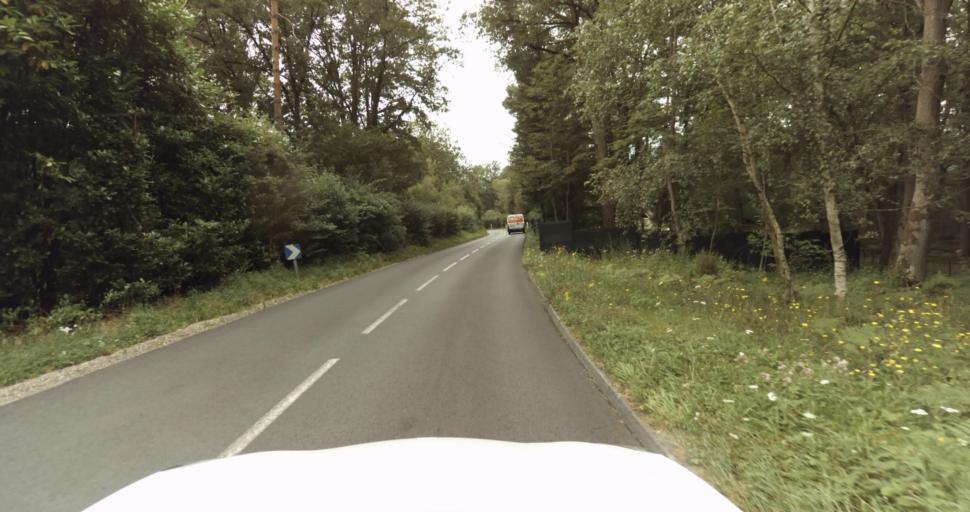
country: FR
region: Haute-Normandie
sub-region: Departement de l'Eure
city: Saint-Sebastien-de-Morsent
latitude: 48.9897
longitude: 1.0556
